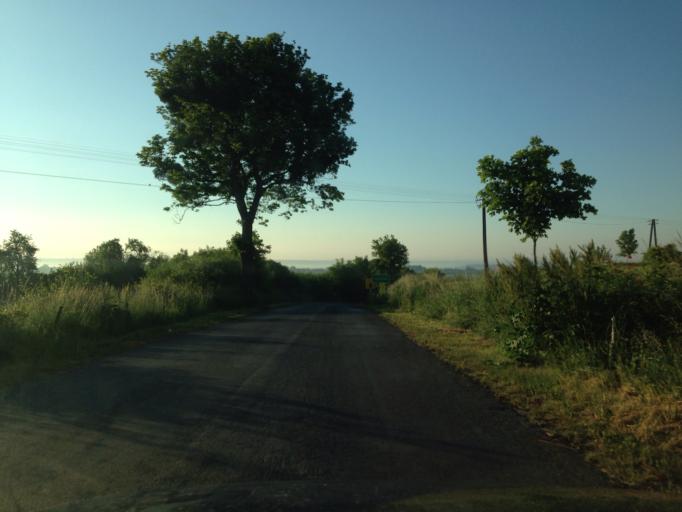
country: PL
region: Pomeranian Voivodeship
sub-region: Powiat tczewski
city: Gniew
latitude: 53.7799
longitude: 18.8291
